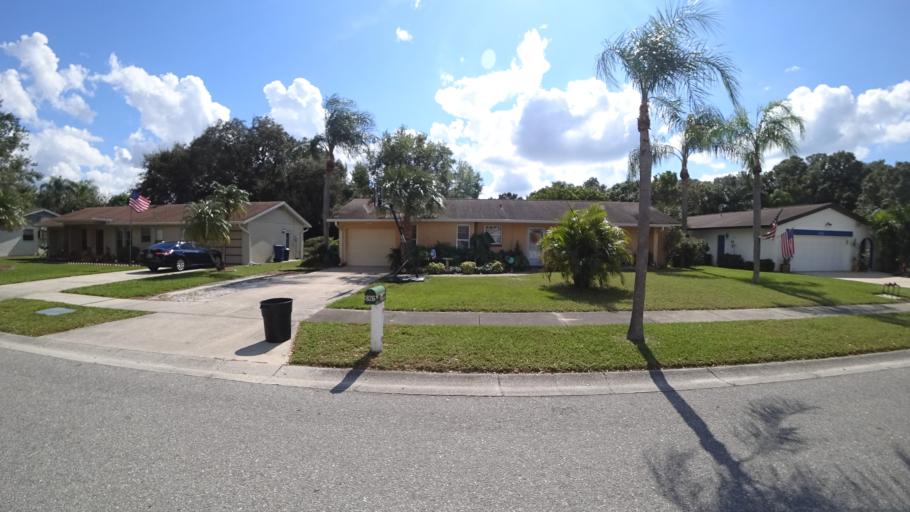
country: US
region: Florida
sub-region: Manatee County
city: Whitfield
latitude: 27.4142
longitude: -82.5573
